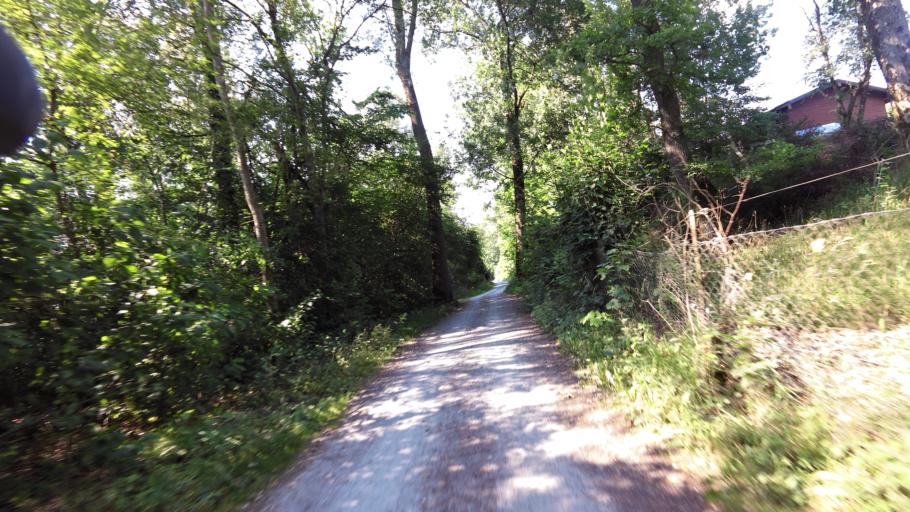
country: DE
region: Bavaria
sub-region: Upper Bavaria
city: Seeon-Seebruck
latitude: 47.9218
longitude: 12.4940
